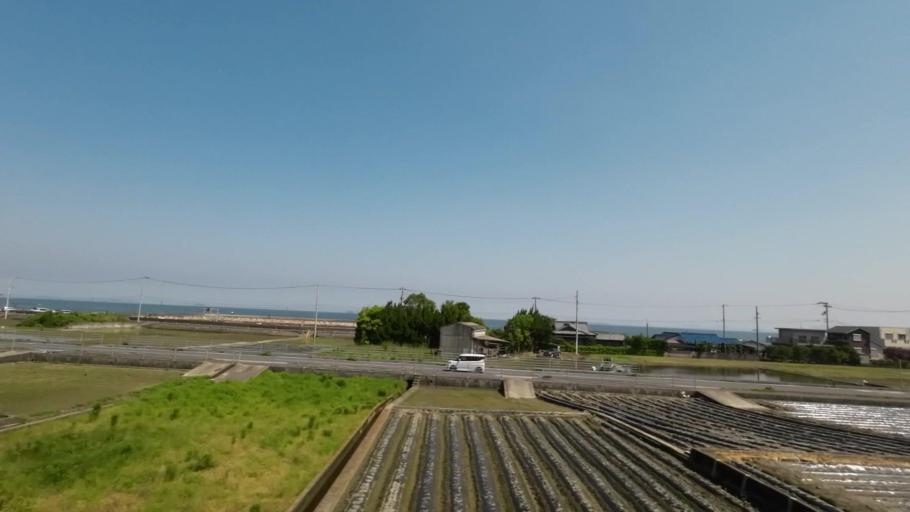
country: JP
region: Ehime
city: Kawanoecho
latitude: 33.9705
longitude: 133.4816
